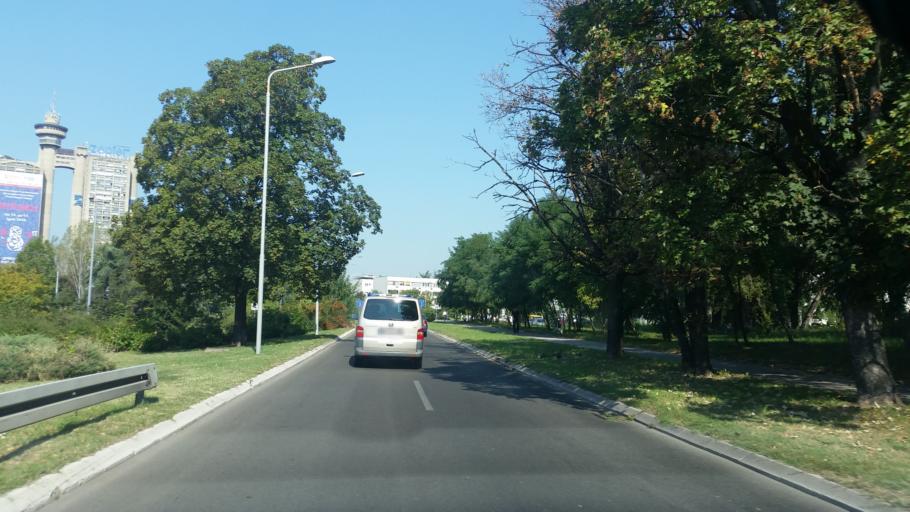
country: RS
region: Central Serbia
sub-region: Belgrade
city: Novi Beograd
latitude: 44.8177
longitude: 20.4097
